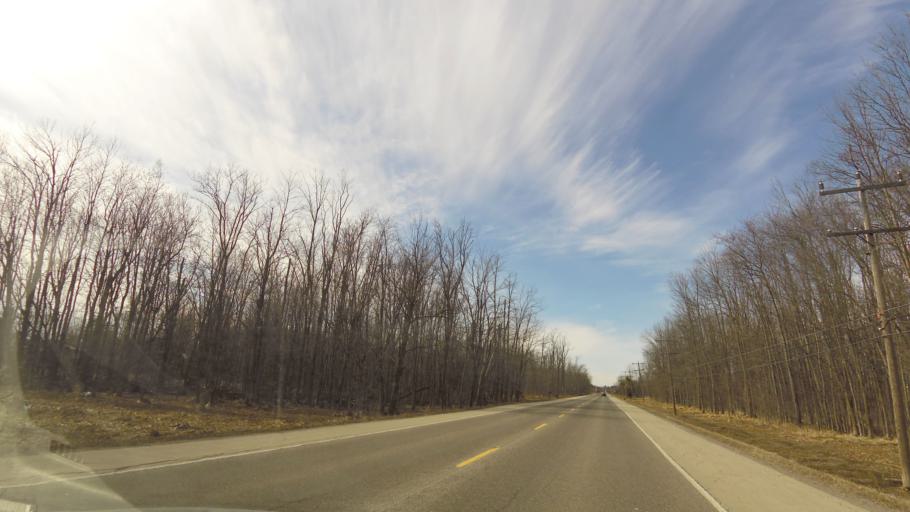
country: CA
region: Ontario
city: Burlington
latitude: 43.3637
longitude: -79.9399
